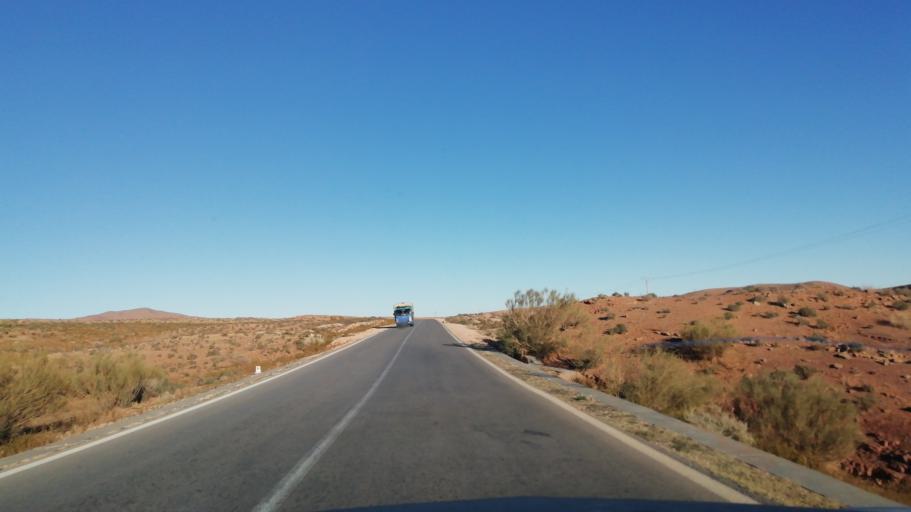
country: DZ
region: El Bayadh
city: El Abiodh Sidi Cheikh
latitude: 33.1658
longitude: 0.4162
